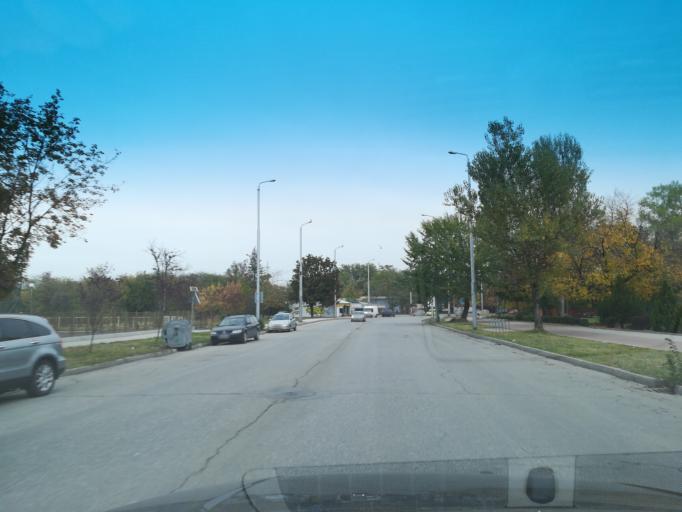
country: BG
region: Plovdiv
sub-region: Obshtina Plovdiv
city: Plovdiv
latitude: 42.1413
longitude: 24.7963
